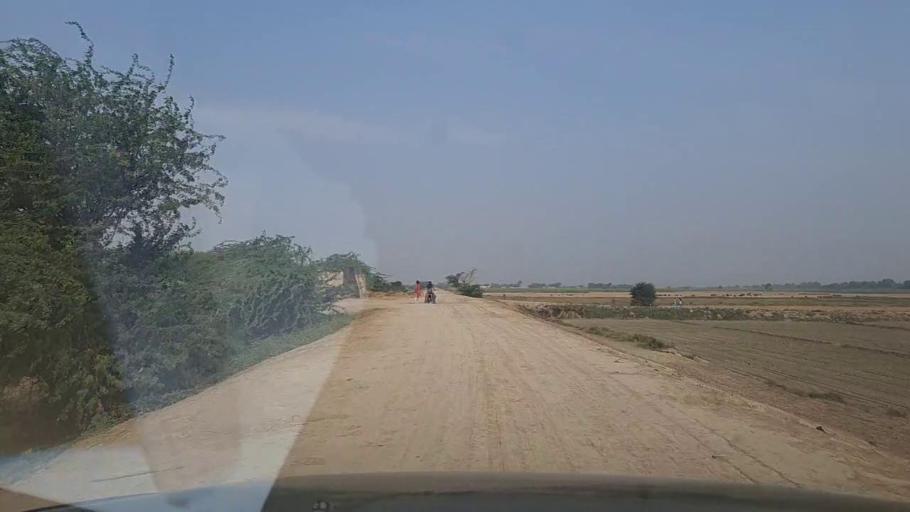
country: PK
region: Sindh
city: Bulri
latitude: 25.0137
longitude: 68.2855
